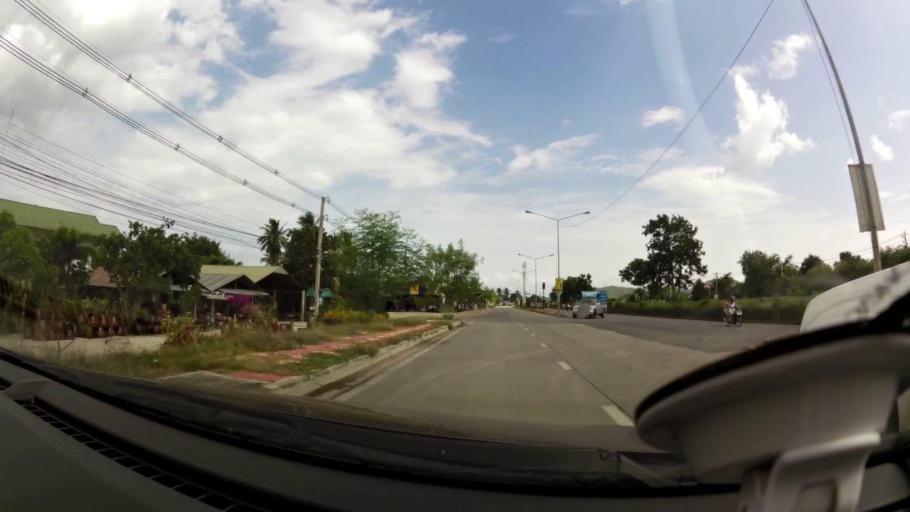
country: TH
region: Prachuap Khiri Khan
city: Hua Hin
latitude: 12.6018
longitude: 99.9452
